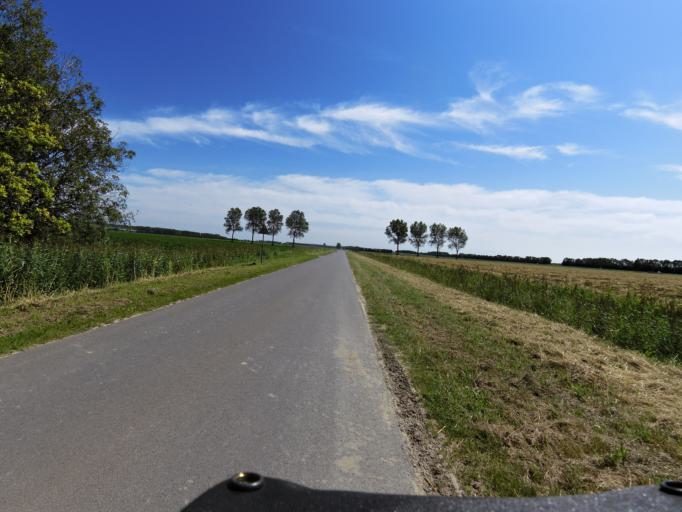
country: NL
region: South Holland
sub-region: Gemeente Goeree-Overflakkee
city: Goedereede
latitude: 51.7941
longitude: 4.0373
